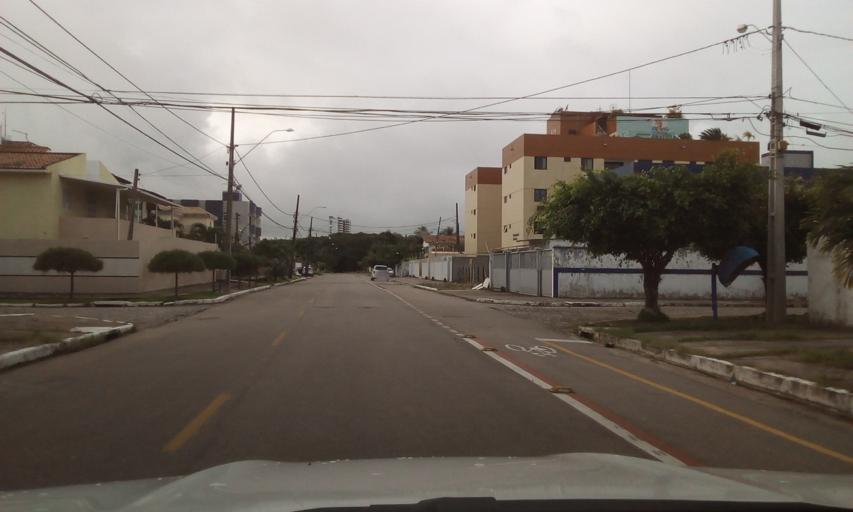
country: BR
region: Paraiba
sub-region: Joao Pessoa
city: Joao Pessoa
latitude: -7.0608
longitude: -34.8453
